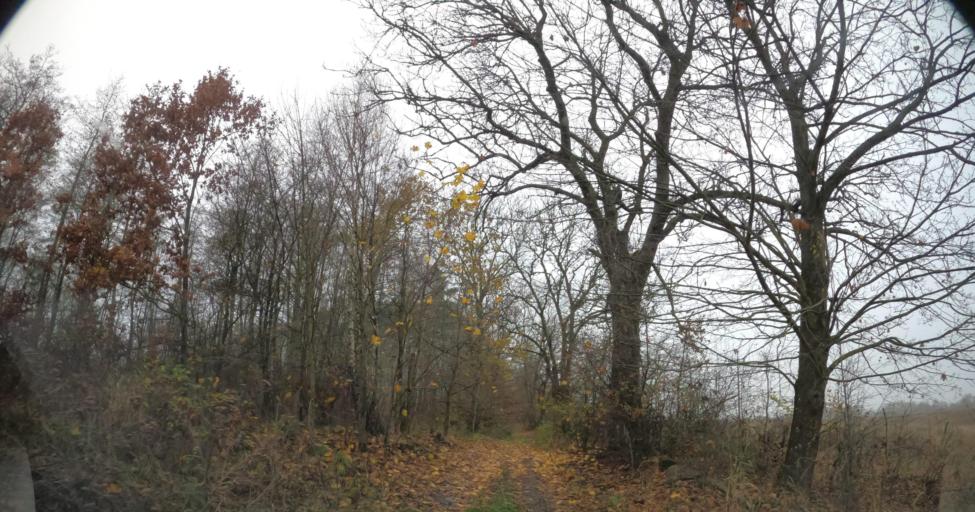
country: PL
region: West Pomeranian Voivodeship
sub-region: Powiat drawski
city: Drawsko Pomorskie
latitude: 53.5961
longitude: 15.7777
